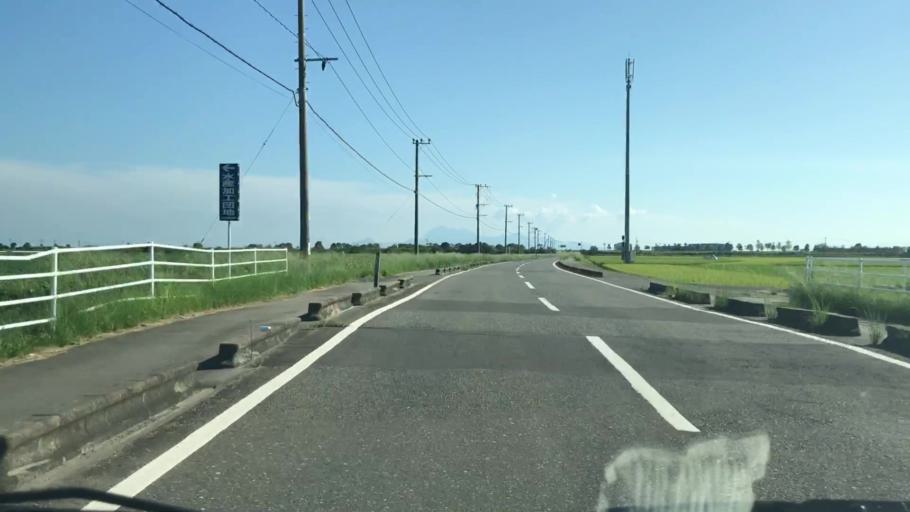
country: JP
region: Saga Prefecture
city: Okawa
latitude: 33.1591
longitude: 130.3086
